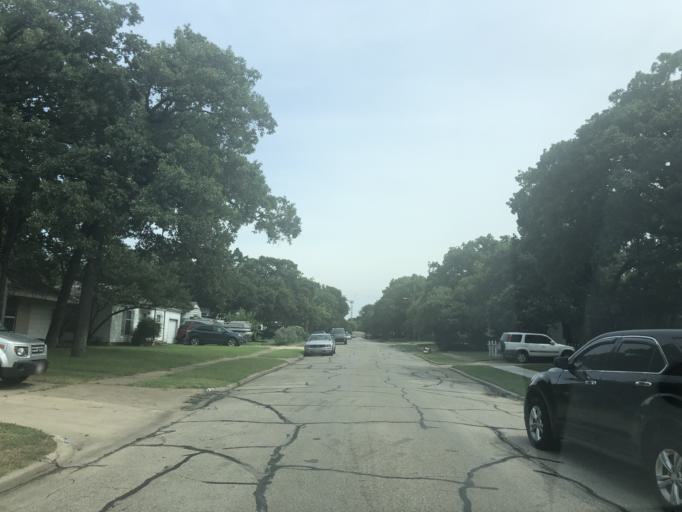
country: US
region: Texas
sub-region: Dallas County
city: Irving
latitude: 32.8117
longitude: -96.9702
